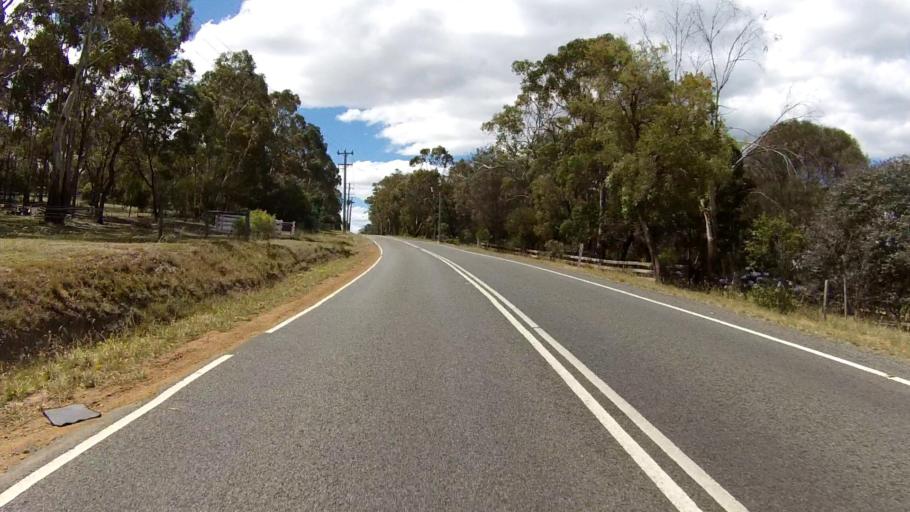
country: AU
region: Tasmania
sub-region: Clarence
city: Lauderdale
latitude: -42.9003
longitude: 147.4796
